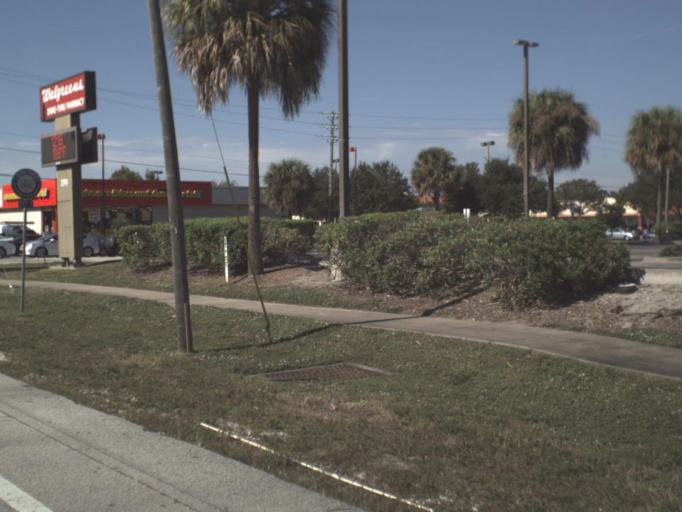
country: US
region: Florida
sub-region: Brevard County
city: Rockledge
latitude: 28.2953
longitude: -80.7215
